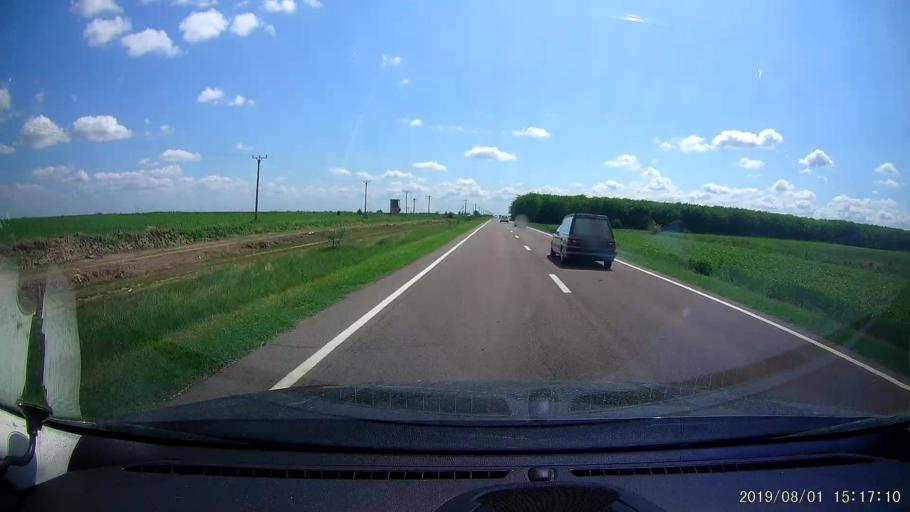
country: RO
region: Braila
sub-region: Comuna Unirea
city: Unirea
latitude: 45.1331
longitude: 27.8405
